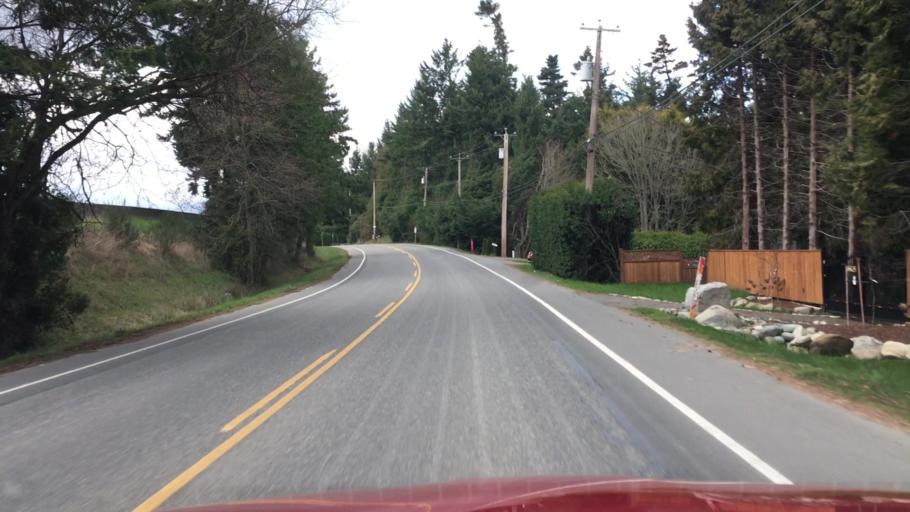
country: CA
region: British Columbia
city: North Saanich
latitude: 48.6047
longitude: -123.3960
